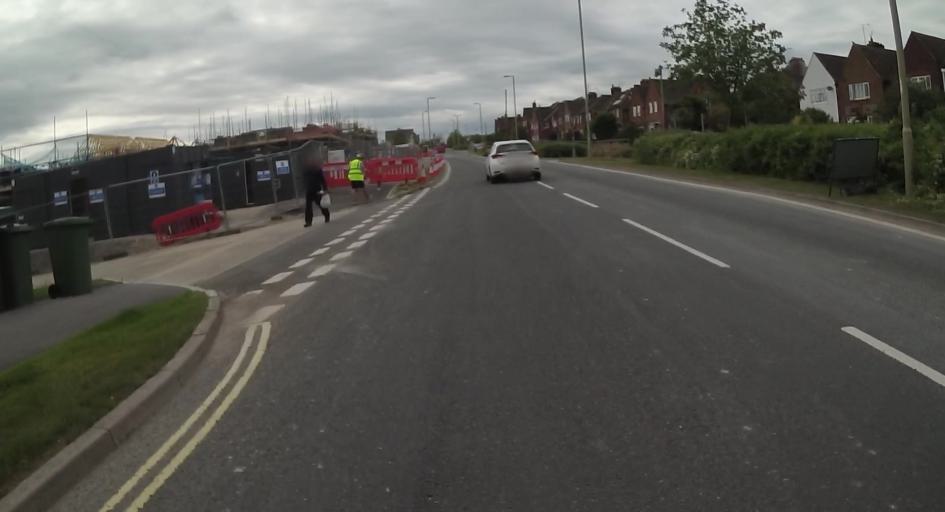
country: GB
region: England
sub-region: Hampshire
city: Basingstoke
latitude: 51.2703
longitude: -1.0944
